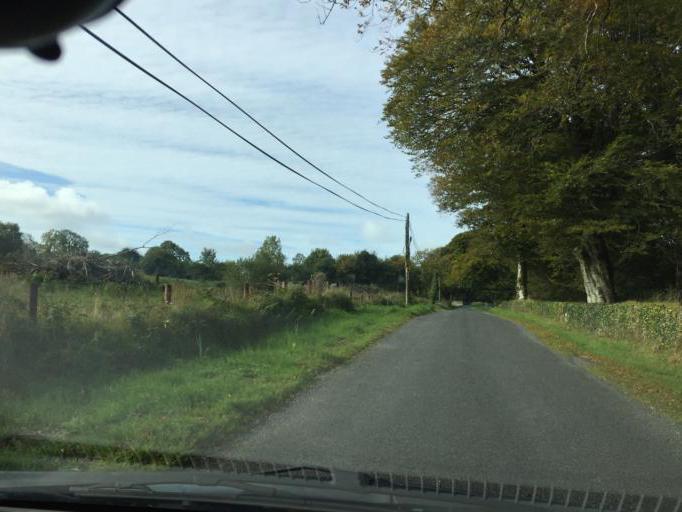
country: IE
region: Connaught
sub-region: Roscommon
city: Boyle
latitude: 54.0297
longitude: -8.2968
